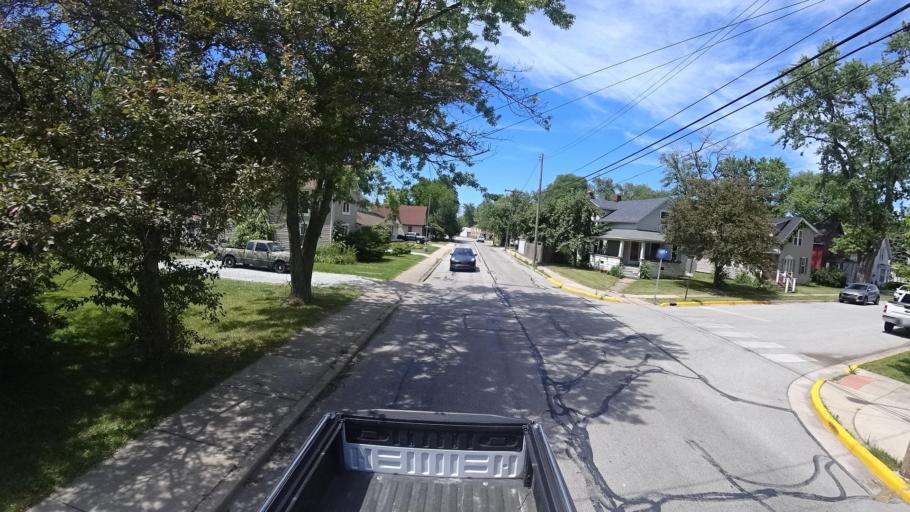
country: US
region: Indiana
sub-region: Porter County
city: Porter
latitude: 41.6157
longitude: -87.0758
